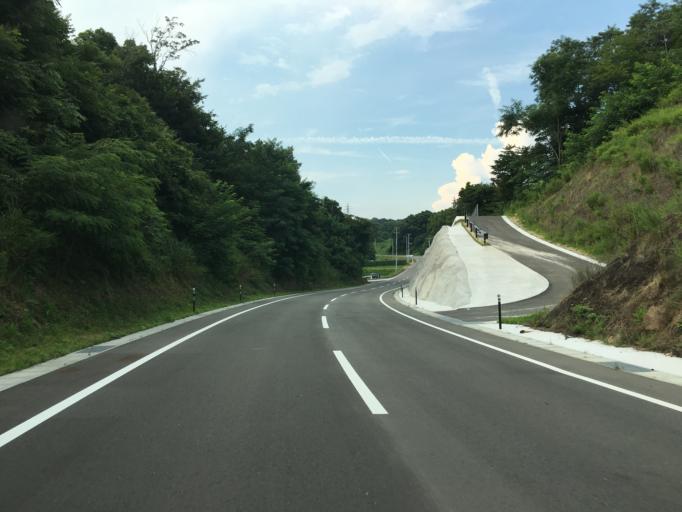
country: JP
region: Fukushima
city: Motomiya
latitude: 37.4846
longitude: 140.4130
